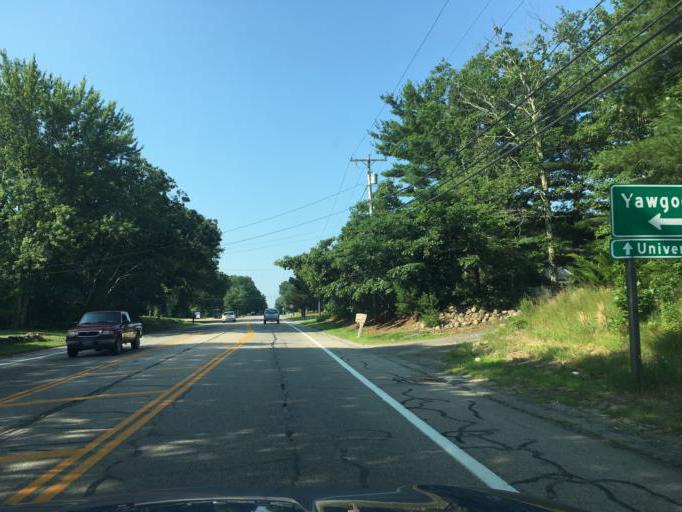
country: US
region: Rhode Island
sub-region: Washington County
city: Kingston
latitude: 41.5233
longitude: -71.5534
